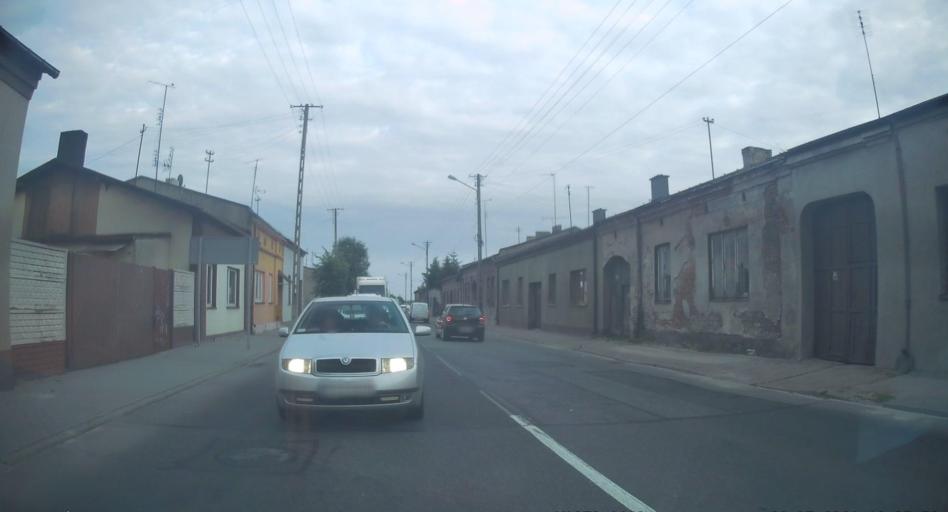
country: PL
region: Lodz Voivodeship
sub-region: Powiat radomszczanski
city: Kamiensk
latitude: 51.2026
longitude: 19.4986
